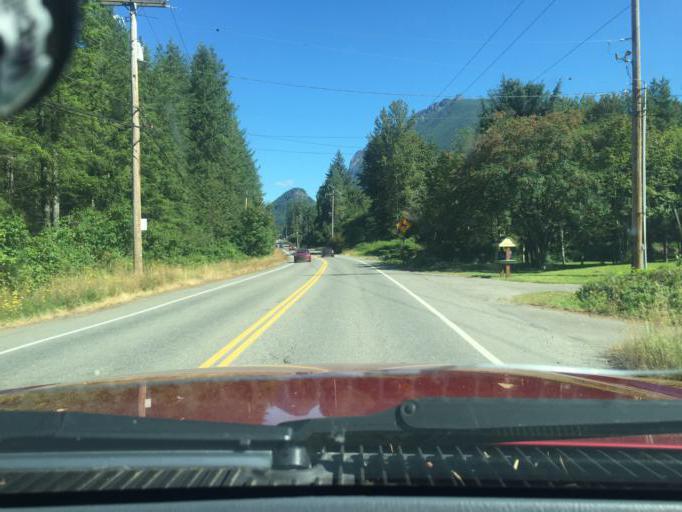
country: US
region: Washington
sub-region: King County
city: Riverbend
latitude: 47.4677
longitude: -121.7586
